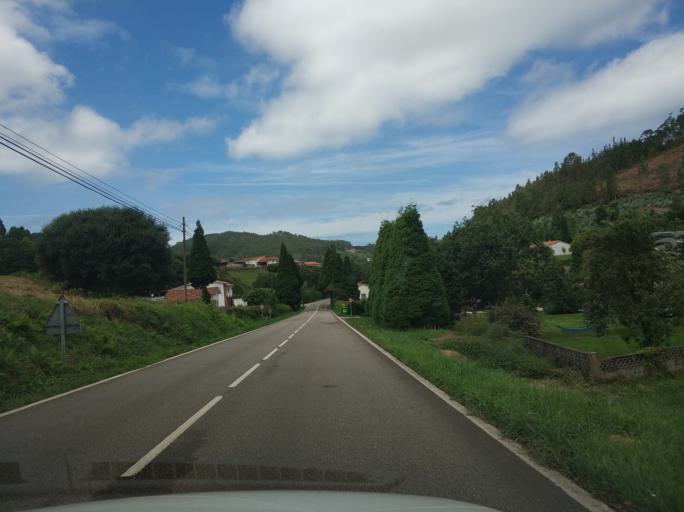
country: ES
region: Asturias
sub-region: Province of Asturias
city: Cudillero
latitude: 43.5498
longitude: -6.2242
